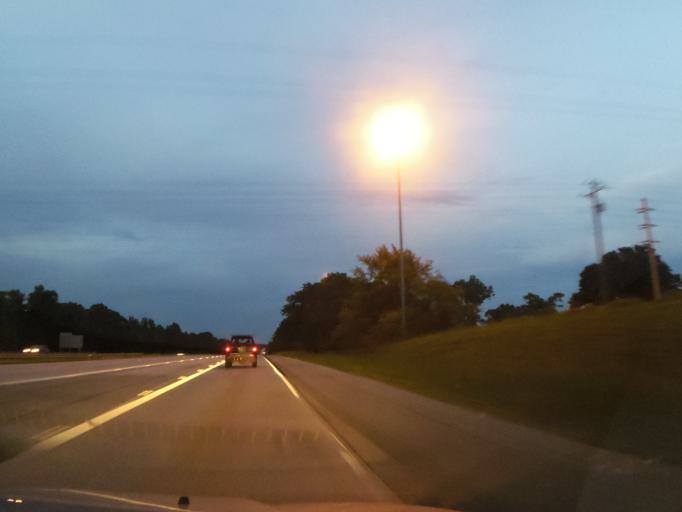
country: US
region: Georgia
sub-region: McDuffie County
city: Thomson
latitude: 33.5117
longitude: -82.4982
